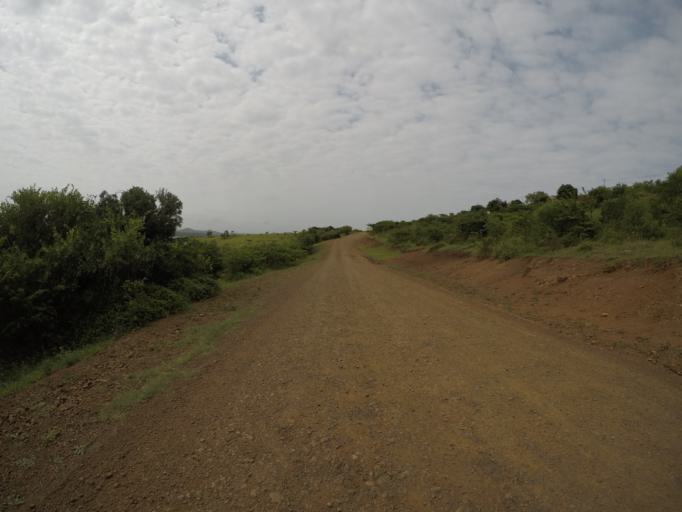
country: ZA
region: KwaZulu-Natal
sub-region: uThungulu District Municipality
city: Empangeni
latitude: -28.6224
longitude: 31.9060
